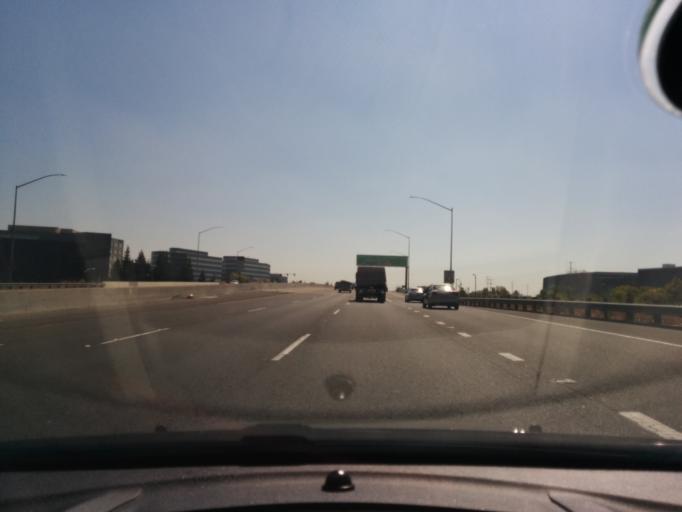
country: US
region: California
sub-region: Santa Clara County
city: Santa Clara
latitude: 37.3687
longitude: -121.9252
